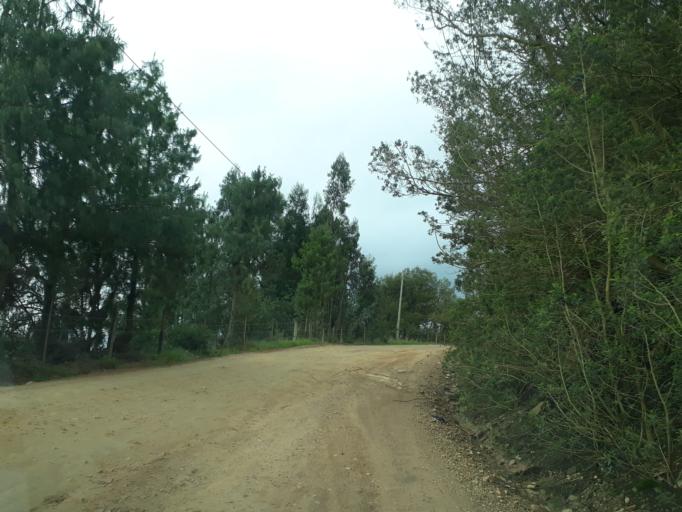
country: CO
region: Cundinamarca
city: Cucunuba
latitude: 5.2025
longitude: -73.7633
